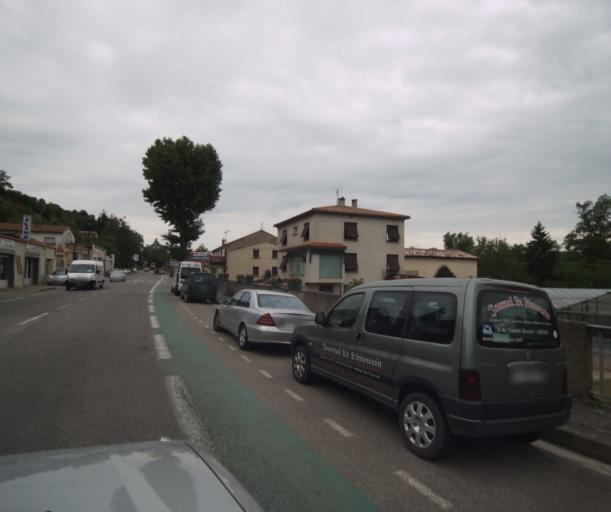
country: FR
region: Languedoc-Roussillon
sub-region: Departement de l'Aude
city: Limoux
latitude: 43.0579
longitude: 2.2136
